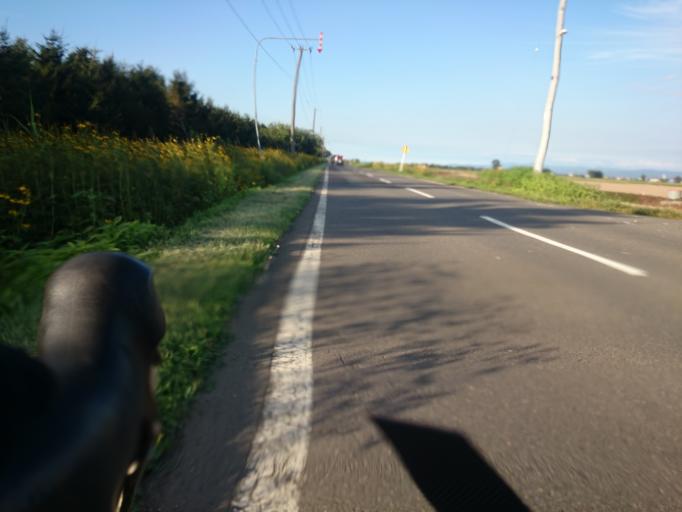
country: JP
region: Hokkaido
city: Tobetsu
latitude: 43.2039
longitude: 141.5798
